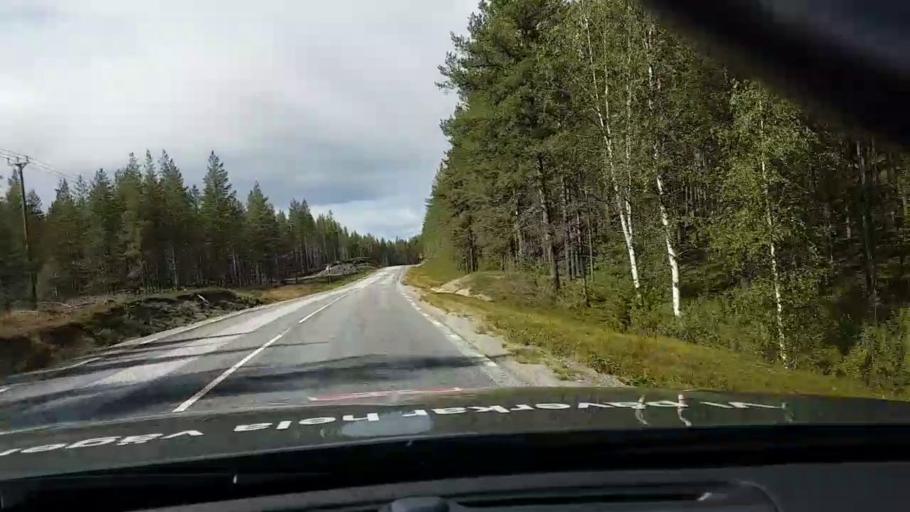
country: SE
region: Vaesterbotten
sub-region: Asele Kommun
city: Asele
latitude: 63.8544
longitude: 17.3900
